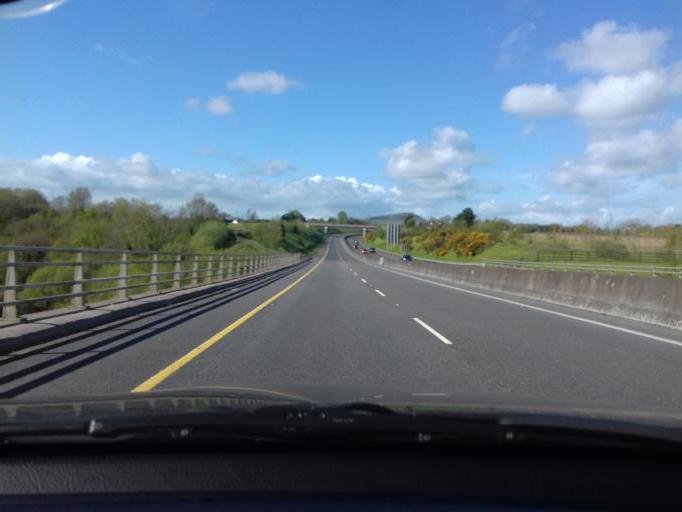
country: IE
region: Munster
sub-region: Waterford
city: Waterford
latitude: 52.2918
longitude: -7.1522
